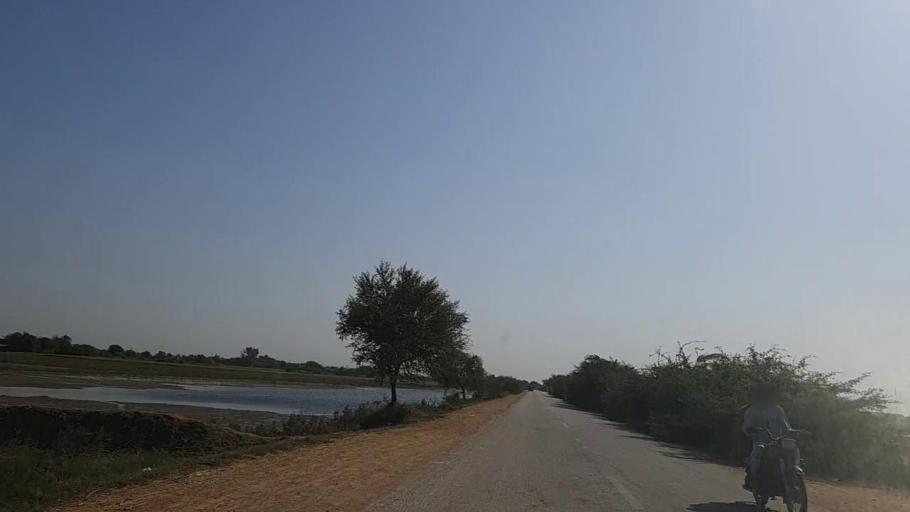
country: PK
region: Sindh
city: Mirpur Batoro
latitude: 24.6109
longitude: 68.2959
